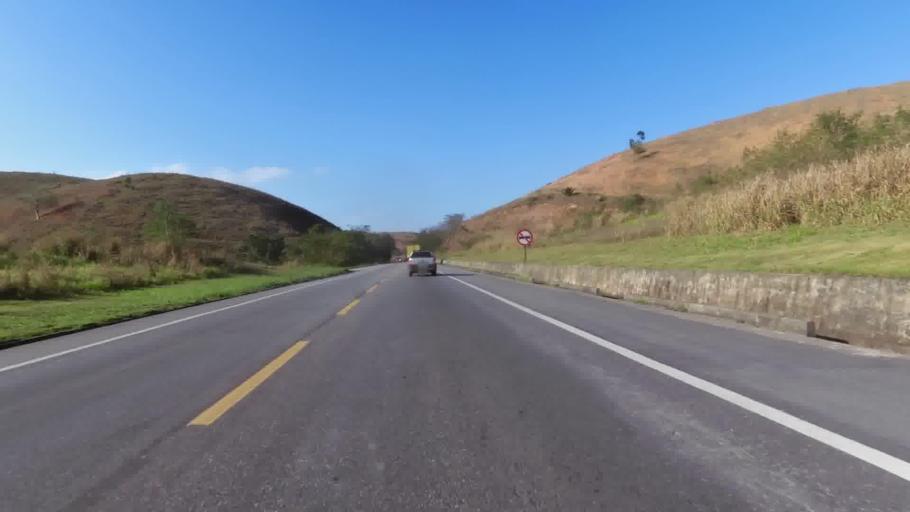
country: BR
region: Espirito Santo
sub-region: Mimoso Do Sul
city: Mimoso do Sul
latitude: -21.1920
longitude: -41.2960
